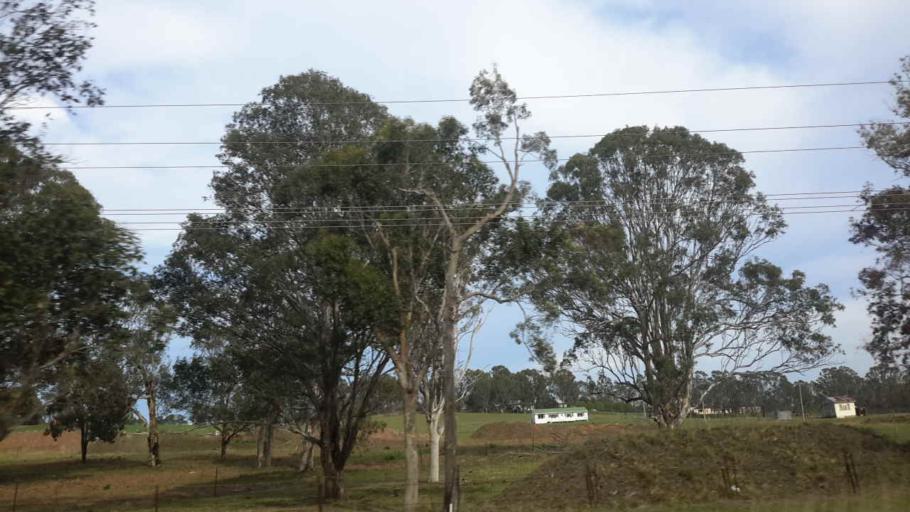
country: AU
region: New South Wales
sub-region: Penrith Municipality
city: Glenmore Park
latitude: -33.8003
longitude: 150.6976
